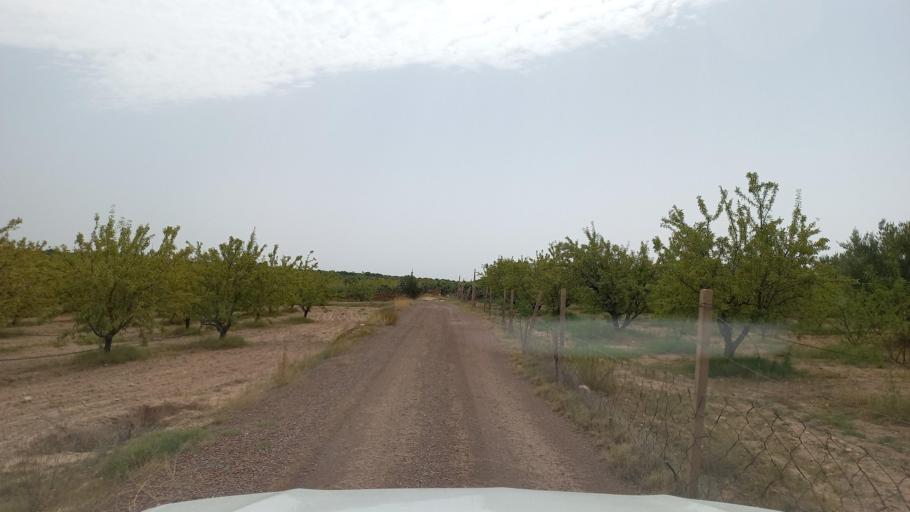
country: TN
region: Al Qasrayn
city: Kasserine
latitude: 35.2691
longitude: 9.0048
